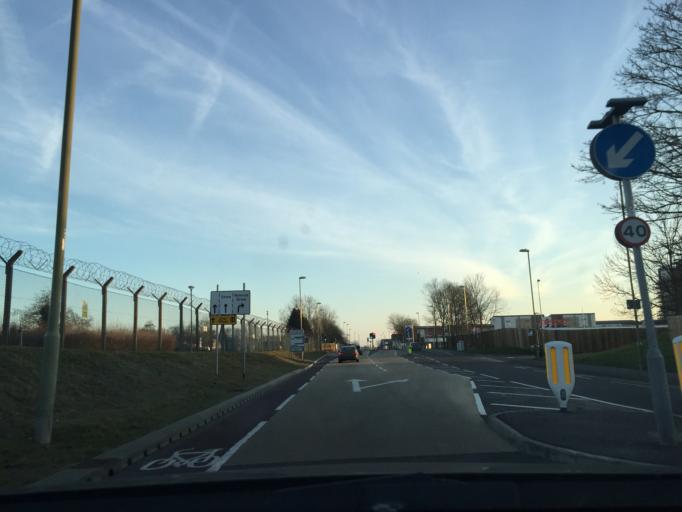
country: GB
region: England
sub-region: Hampshire
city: Lee-on-the-Solent
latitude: 50.8045
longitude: -1.1652
